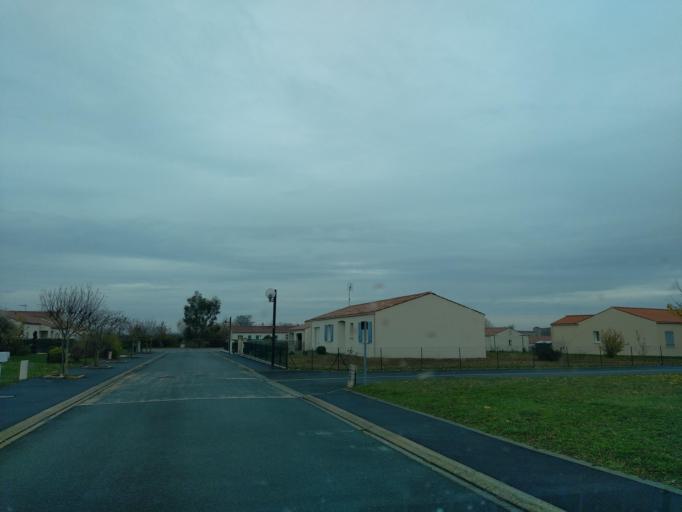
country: FR
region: Pays de la Loire
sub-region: Departement de la Vendee
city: Maillezais
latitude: 46.3679
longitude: -0.7421
